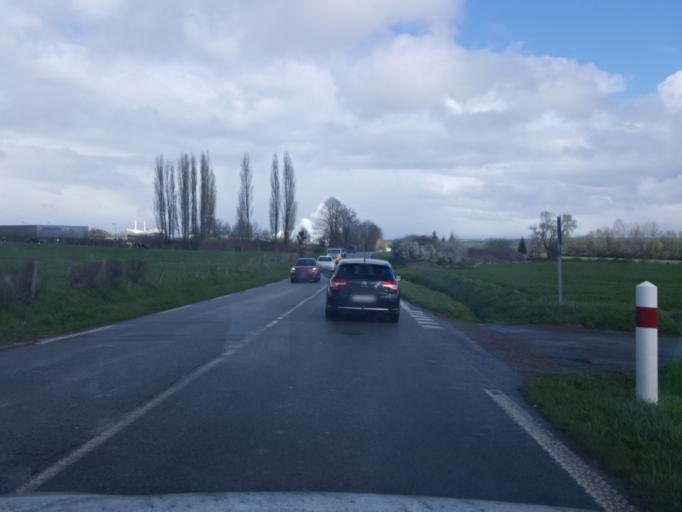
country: FR
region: Picardie
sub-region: Departement de l'Oise
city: Auneuil
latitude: 49.3785
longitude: 1.9939
